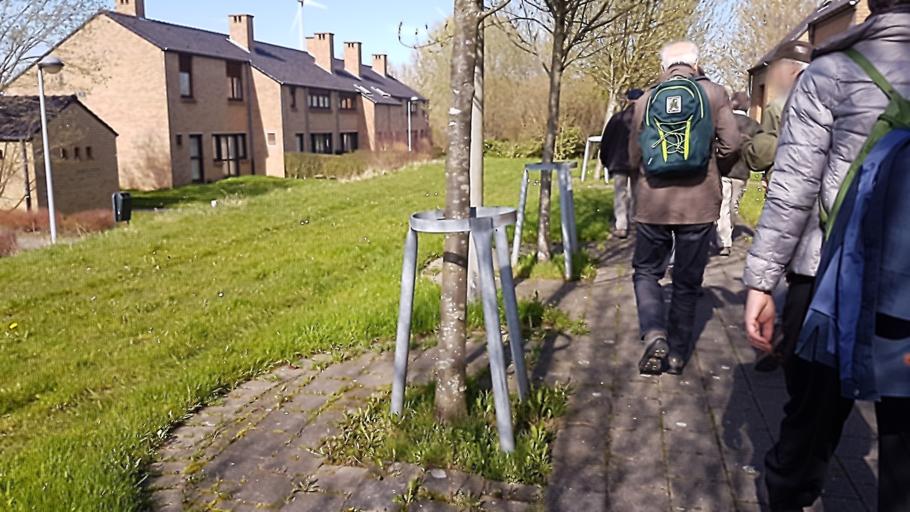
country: BE
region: Flanders
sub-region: Provincie West-Vlaanderen
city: Zwevegem
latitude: 50.8122
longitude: 3.3026
